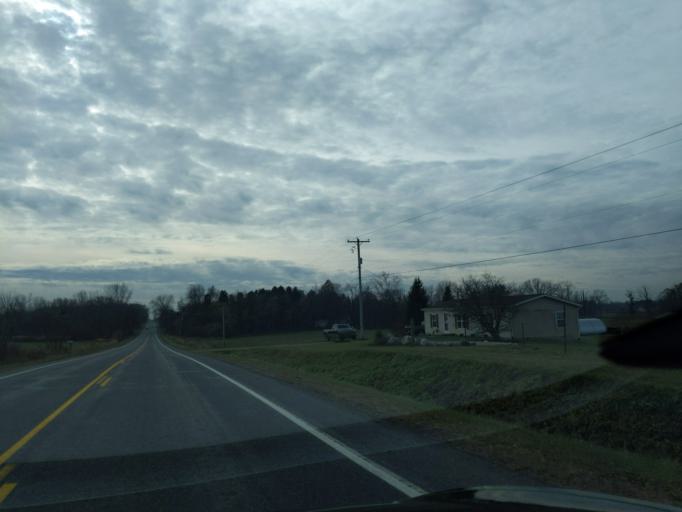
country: US
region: Michigan
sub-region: Ingham County
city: Holt
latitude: 42.6062
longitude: -84.5231
